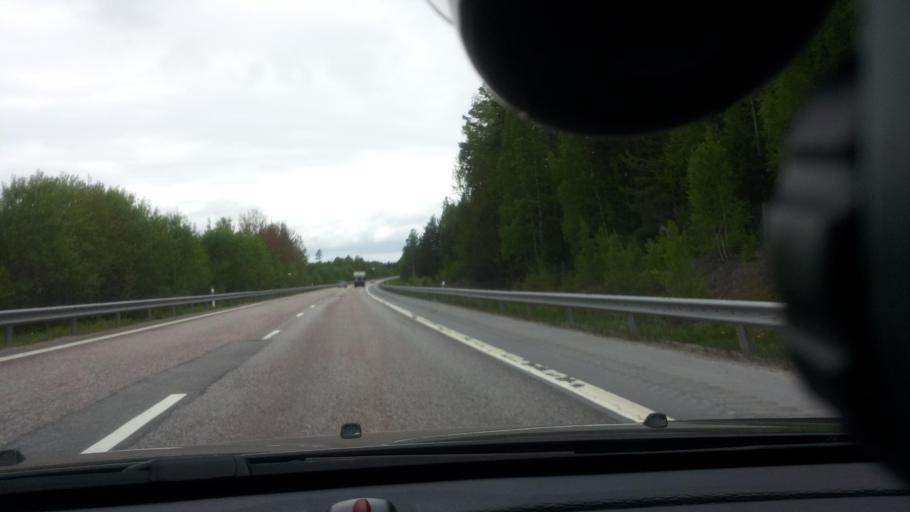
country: SE
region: Uppsala
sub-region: Alvkarleby Kommun
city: AElvkarleby
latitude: 60.4737
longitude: 17.3850
